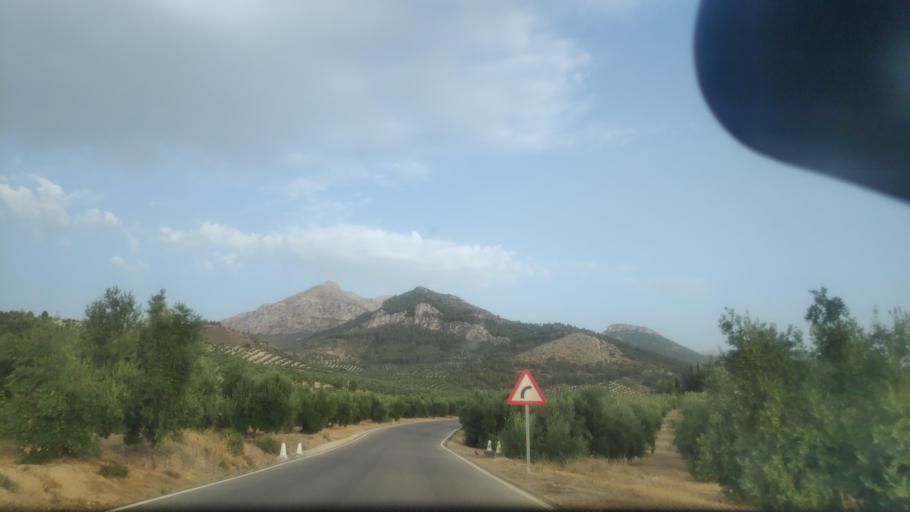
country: ES
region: Andalusia
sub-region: Provincia de Jaen
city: Jimena
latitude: 37.8353
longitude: -3.5294
